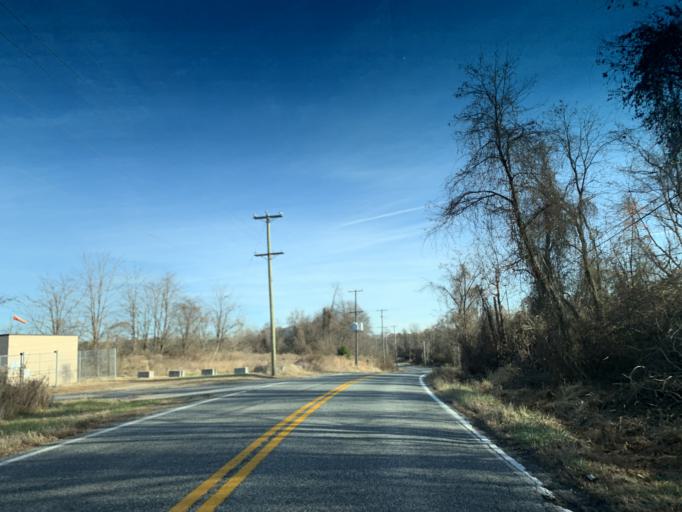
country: US
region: Maryland
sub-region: Cecil County
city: Charlestown
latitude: 39.5784
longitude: -75.9989
